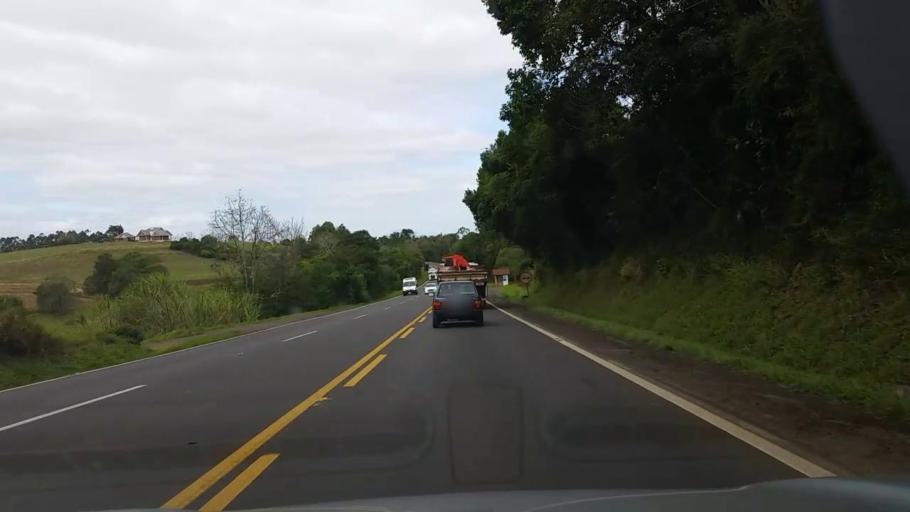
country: BR
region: Rio Grande do Sul
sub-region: Arroio Do Meio
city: Arroio do Meio
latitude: -29.3979
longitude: -52.0415
